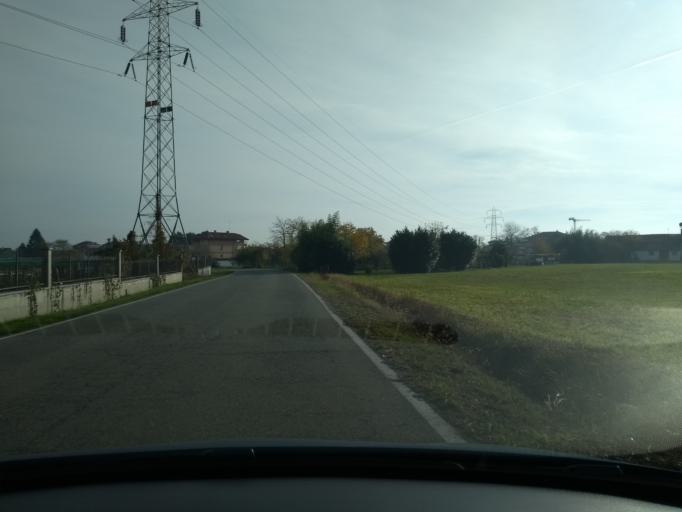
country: IT
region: Piedmont
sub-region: Provincia di Torino
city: Mathi
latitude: 45.2641
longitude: 7.5335
